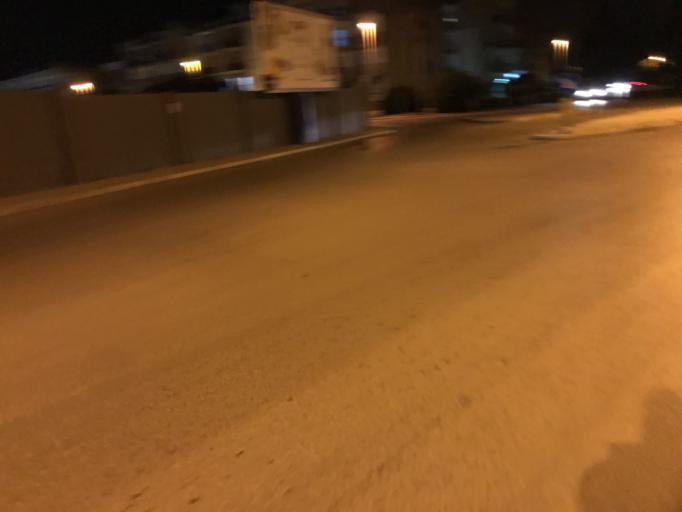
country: IT
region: Apulia
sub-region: Provincia di Bari
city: Corato
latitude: 41.1562
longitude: 16.4022
